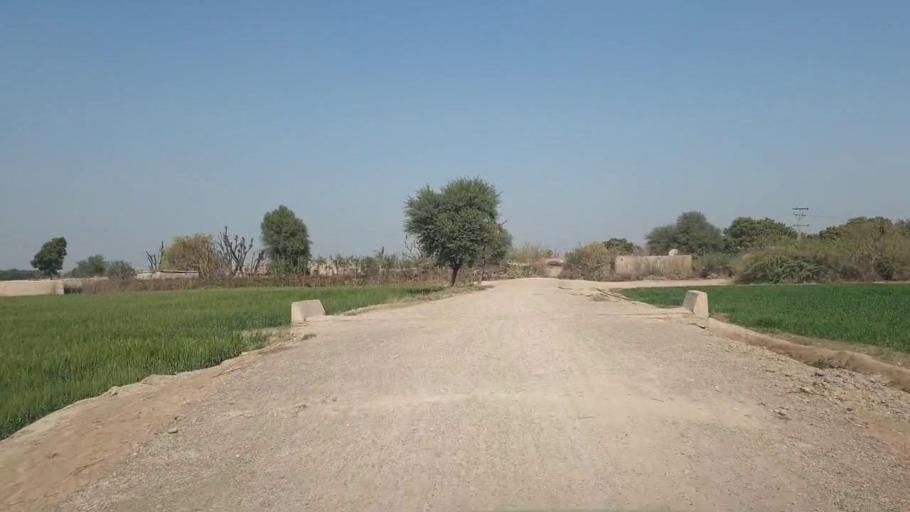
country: PK
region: Sindh
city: Tando Jam
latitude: 25.3030
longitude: 68.6454
